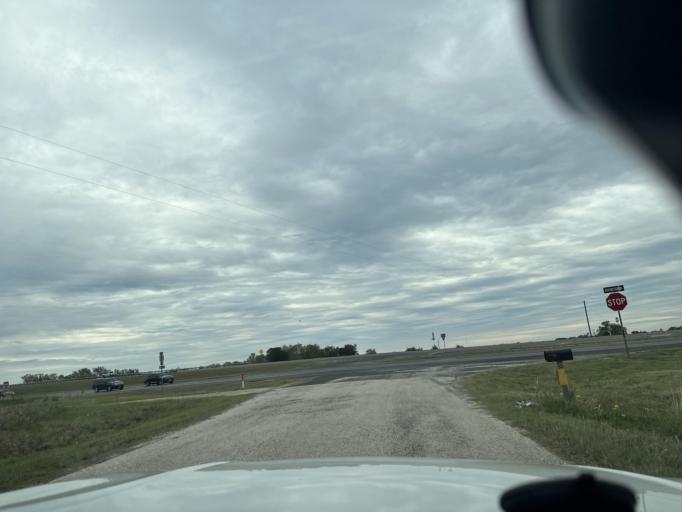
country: US
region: Texas
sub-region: Burleson County
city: Somerville
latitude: 30.1515
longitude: -96.6332
